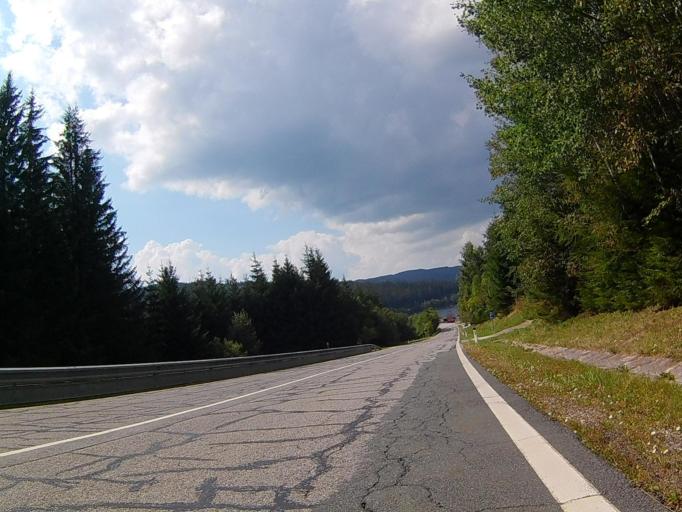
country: AT
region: Styria
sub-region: Politischer Bezirk Deutschlandsberg
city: Soboth
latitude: 46.6761
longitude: 15.0420
